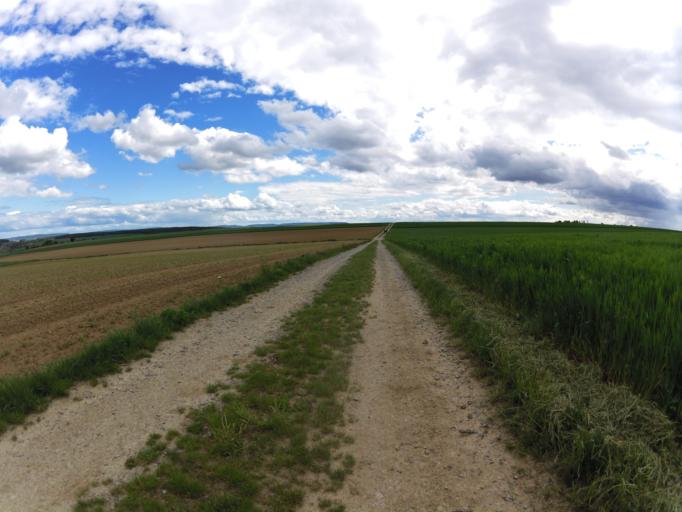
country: DE
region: Bavaria
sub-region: Regierungsbezirk Unterfranken
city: Volkach
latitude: 49.8835
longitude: 10.2328
